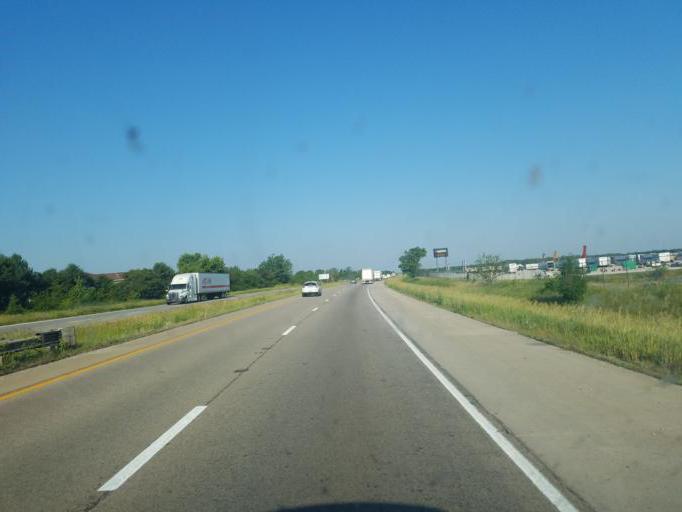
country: US
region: Illinois
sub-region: Grundy County
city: Morris
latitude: 41.3788
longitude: -88.4445
